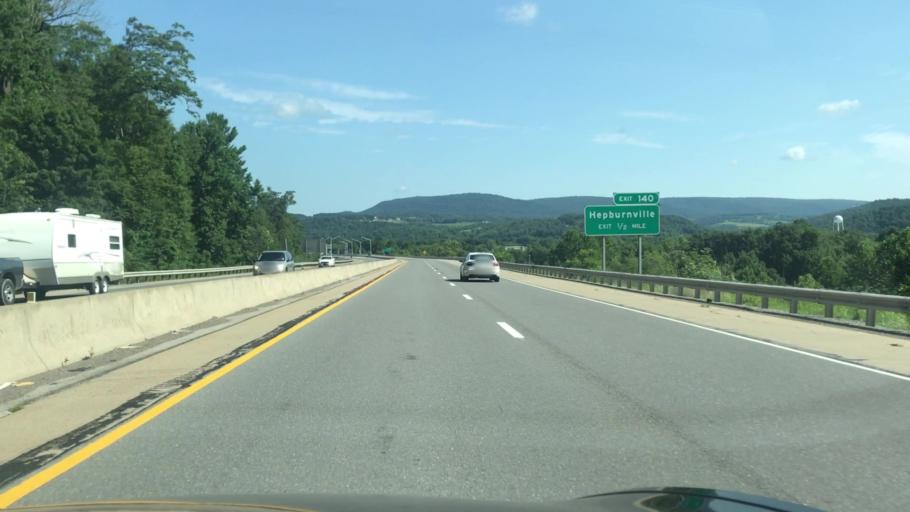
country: US
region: Pennsylvania
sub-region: Lycoming County
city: Garden View
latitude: 41.2828
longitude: -77.0644
